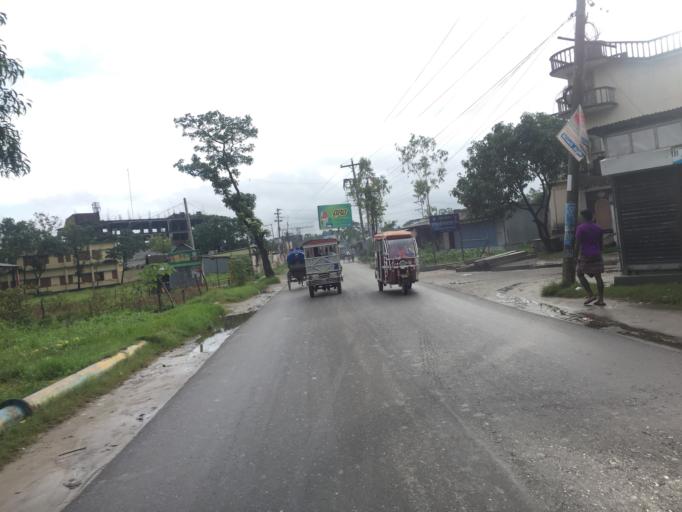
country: BD
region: Dhaka
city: Narayanganj
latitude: 23.5576
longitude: 90.5082
